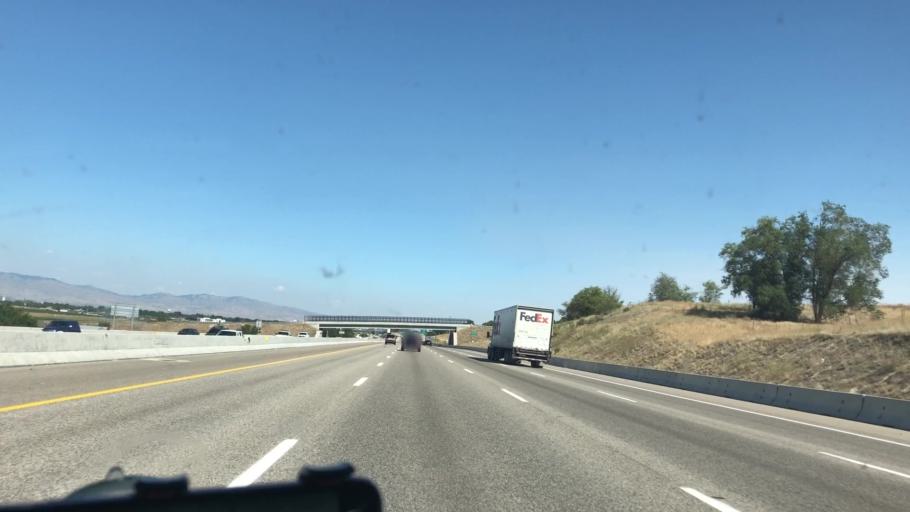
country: US
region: Idaho
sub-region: Ada County
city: Meridian
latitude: 43.5952
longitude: -116.4582
